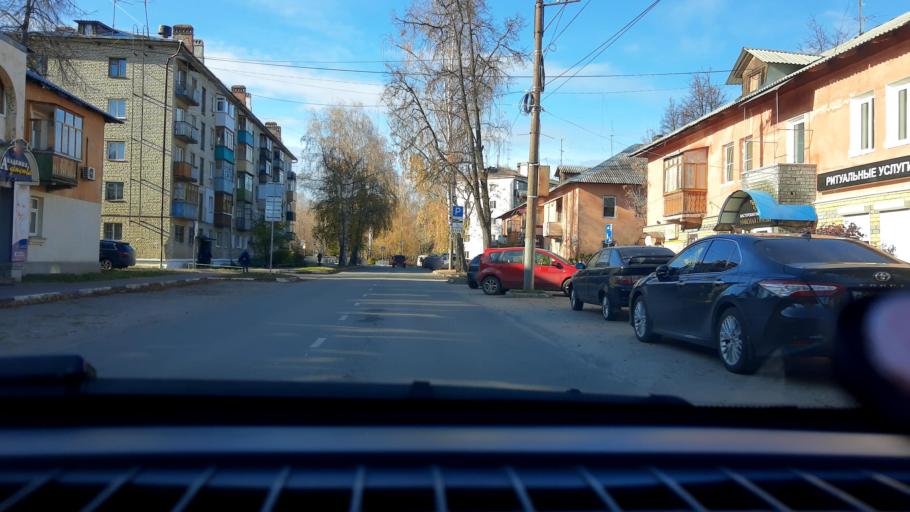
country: RU
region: Nizjnij Novgorod
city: Kstovo
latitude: 56.1450
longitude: 44.2039
